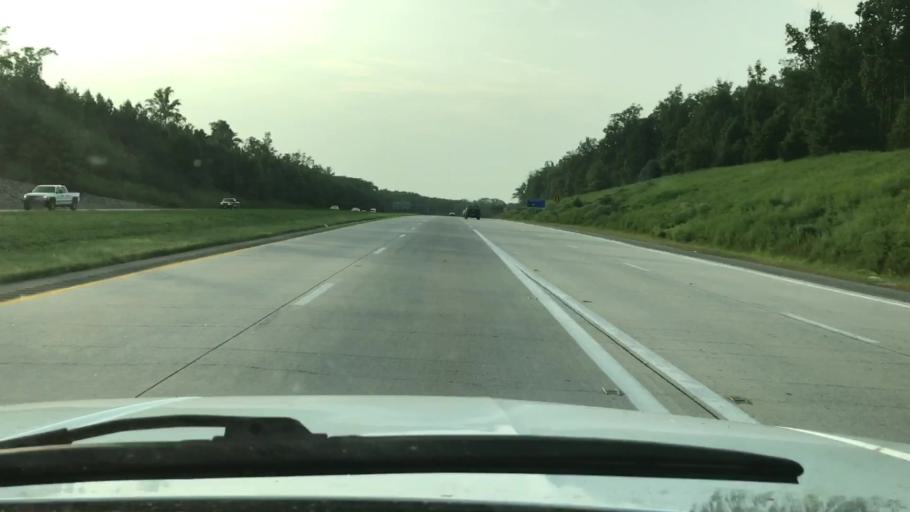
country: US
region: Virginia
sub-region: Chesterfield County
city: Brandermill
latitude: 37.4726
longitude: -77.6545
